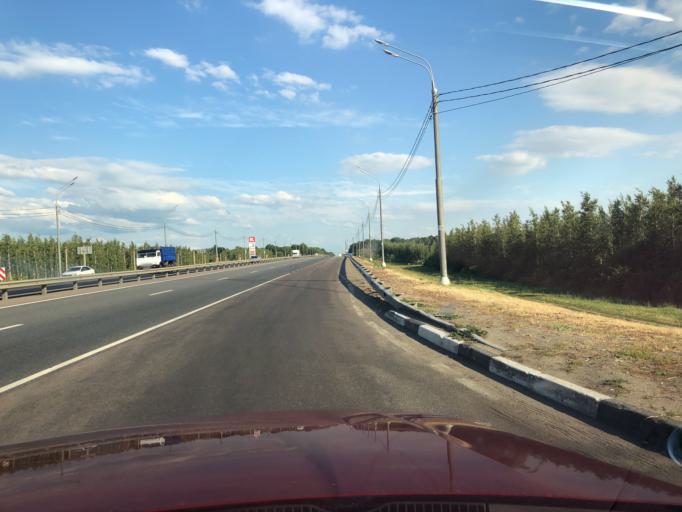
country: RU
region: Lipetsk
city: Zadonsk
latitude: 52.4260
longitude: 38.8294
